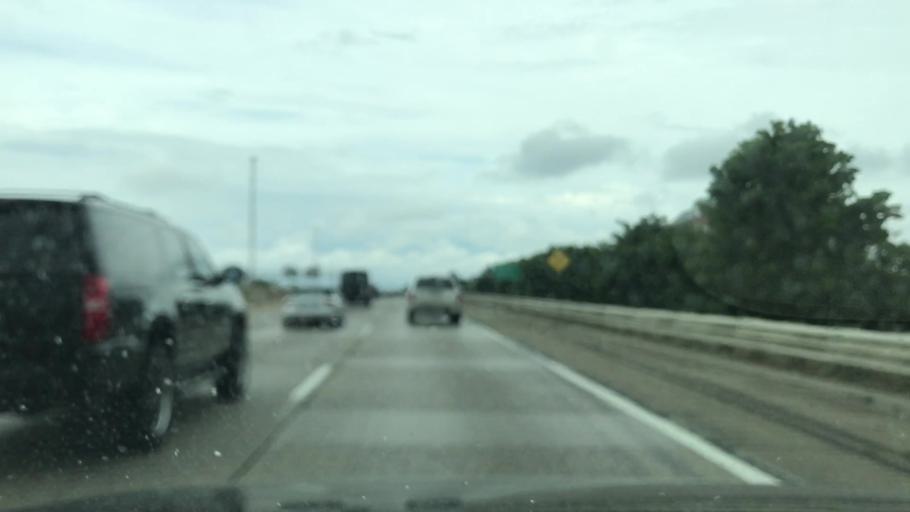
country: US
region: Michigan
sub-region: Kent County
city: Grand Rapids
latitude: 42.9830
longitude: -85.6770
